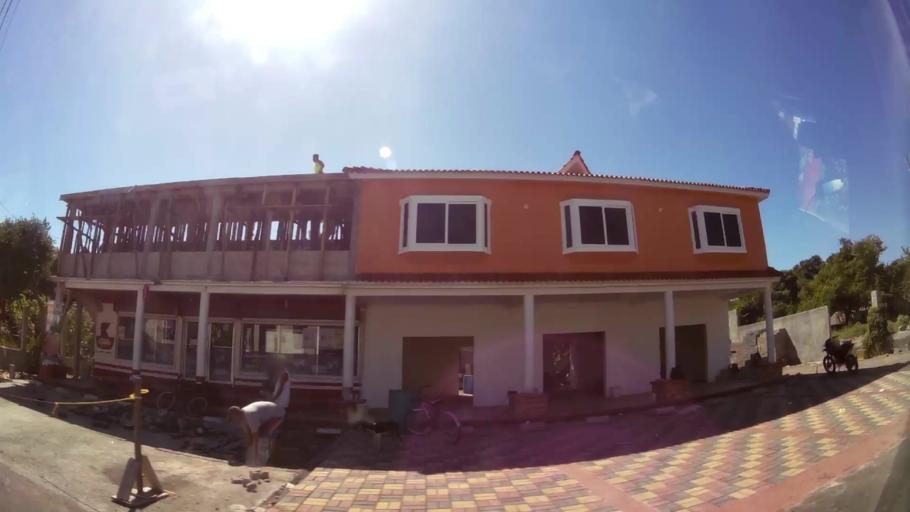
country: GT
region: Escuintla
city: Iztapa
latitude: 13.9328
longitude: -90.6833
